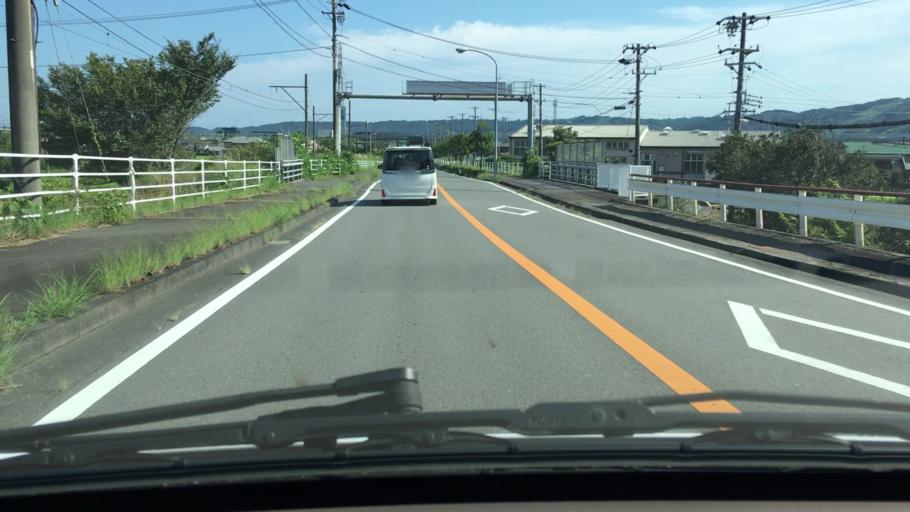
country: JP
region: Shizuoka
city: Kanaya
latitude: 34.8559
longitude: 138.1155
